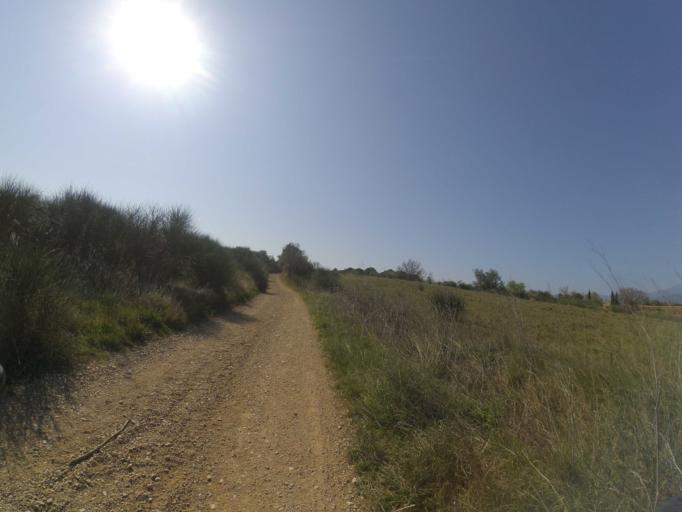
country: FR
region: Languedoc-Roussillon
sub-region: Departement des Pyrenees-Orientales
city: Llupia
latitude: 42.6129
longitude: 2.7636
